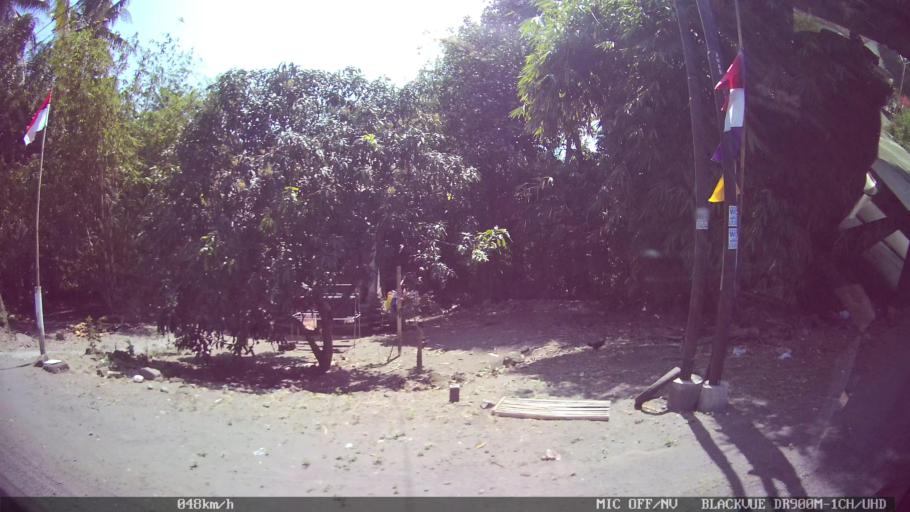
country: ID
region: Daerah Istimewa Yogyakarta
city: Srandakan
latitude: -7.9215
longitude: 110.1144
